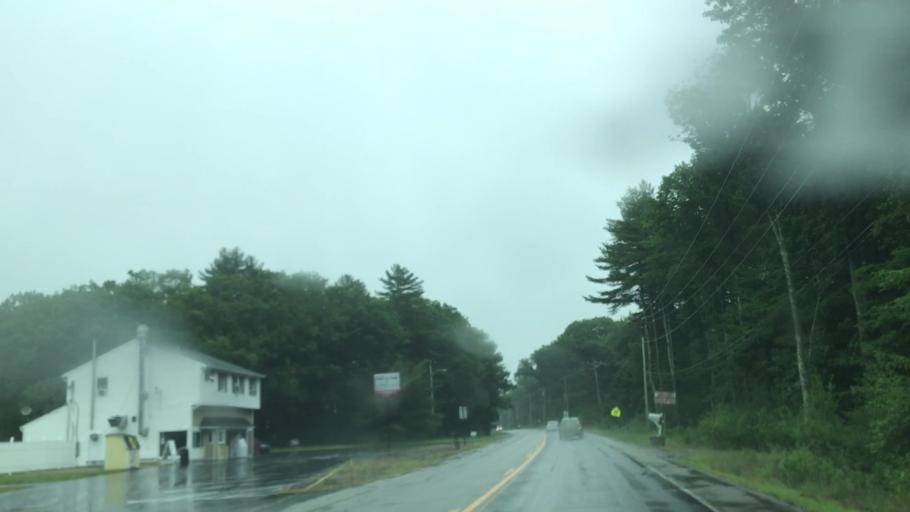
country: US
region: Maine
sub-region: York County
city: Berwick
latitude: 43.2851
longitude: -70.8231
